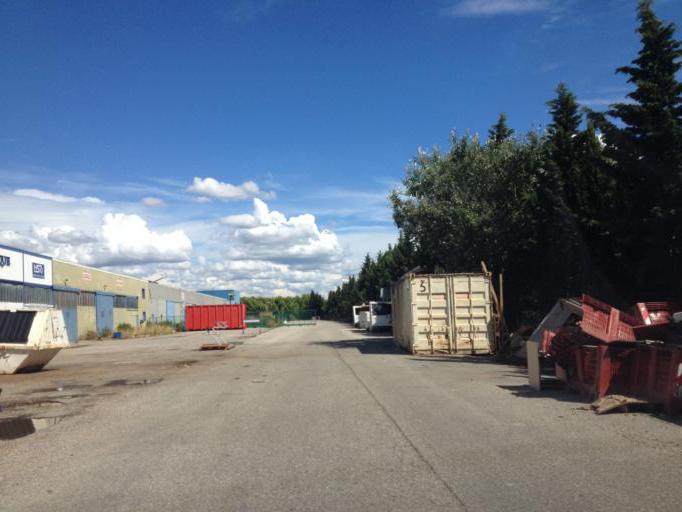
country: FR
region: Provence-Alpes-Cote d'Azur
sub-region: Departement du Vaucluse
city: Orange
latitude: 44.1108
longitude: 4.8394
